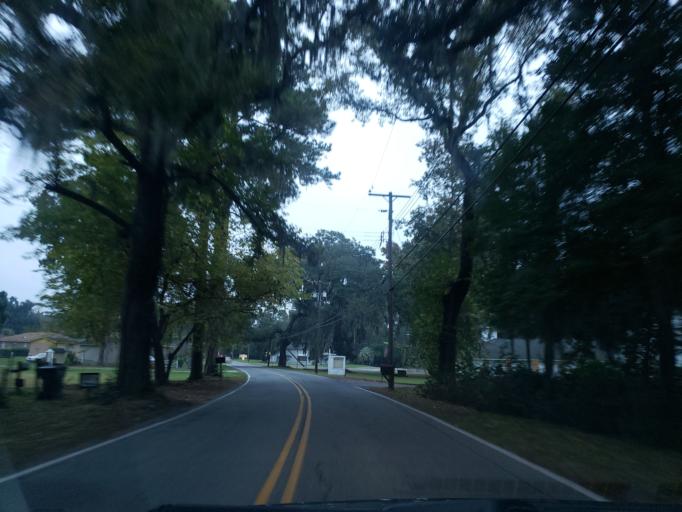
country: US
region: Georgia
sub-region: Chatham County
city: Thunderbolt
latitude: 32.0121
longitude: -81.0650
